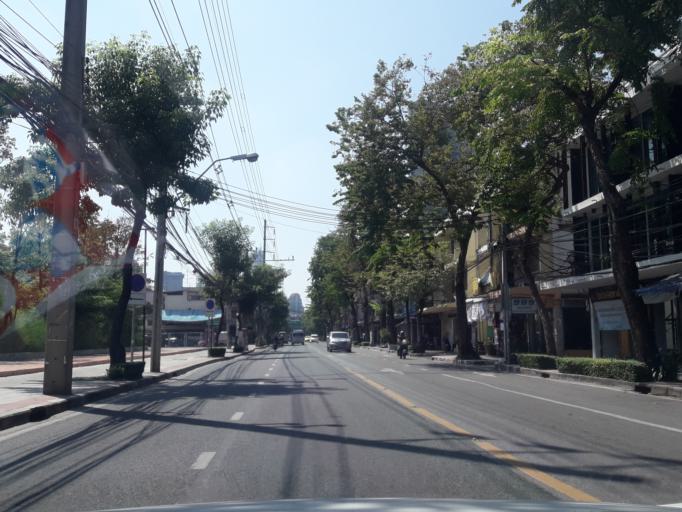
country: TH
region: Bangkok
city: Pathum Wan
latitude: 13.7398
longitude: 100.5224
